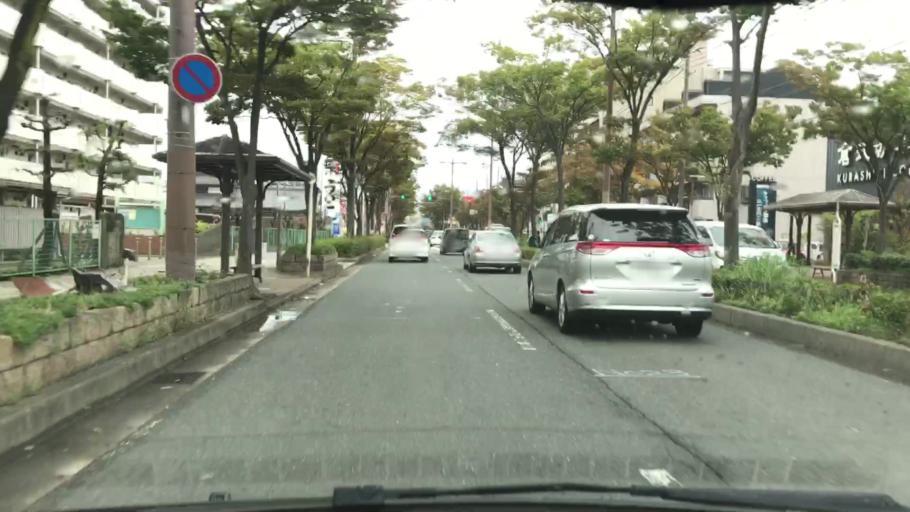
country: JP
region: Hyogo
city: Amagasaki
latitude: 34.7444
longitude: 135.4019
